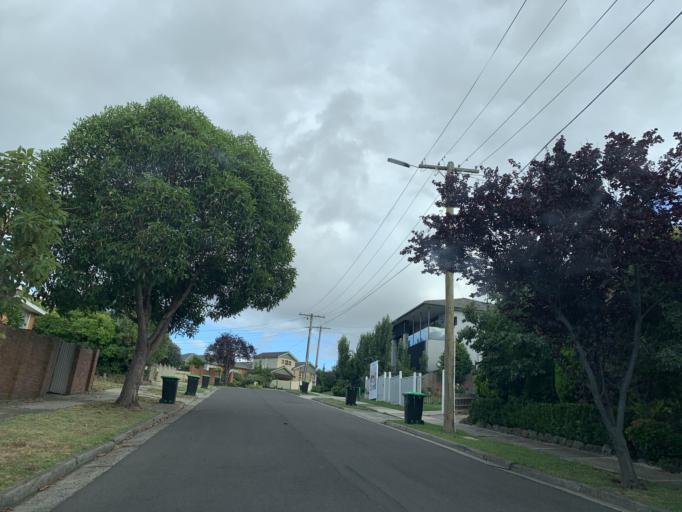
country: AU
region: Victoria
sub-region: Moreland
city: Gowanbrae
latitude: -37.7112
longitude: 144.8946
